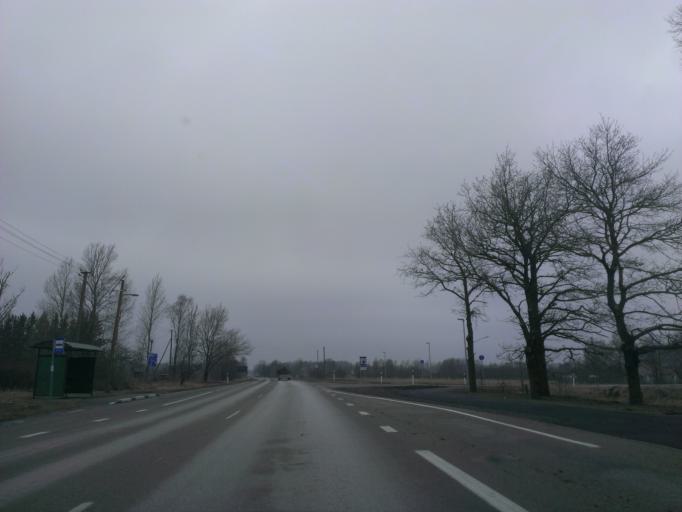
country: EE
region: Paernumaa
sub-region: Audru vald
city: Audru
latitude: 58.4714
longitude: 24.1960
